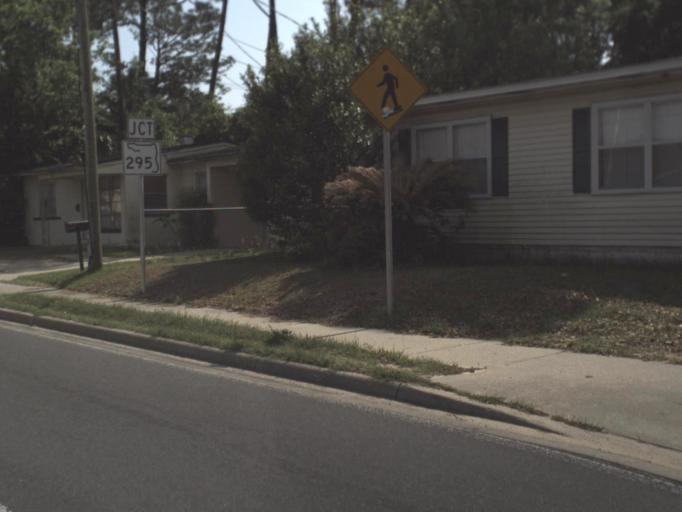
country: US
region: Florida
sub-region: Escambia County
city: Goulding
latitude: 30.4553
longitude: -87.2146
